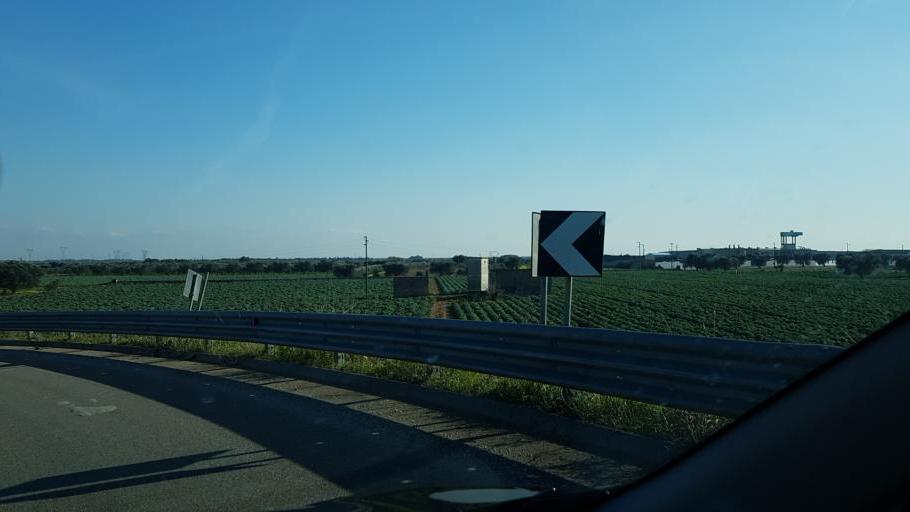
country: IT
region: Apulia
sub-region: Provincia di Brindisi
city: Mesagne
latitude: 40.5750
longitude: 17.8333
